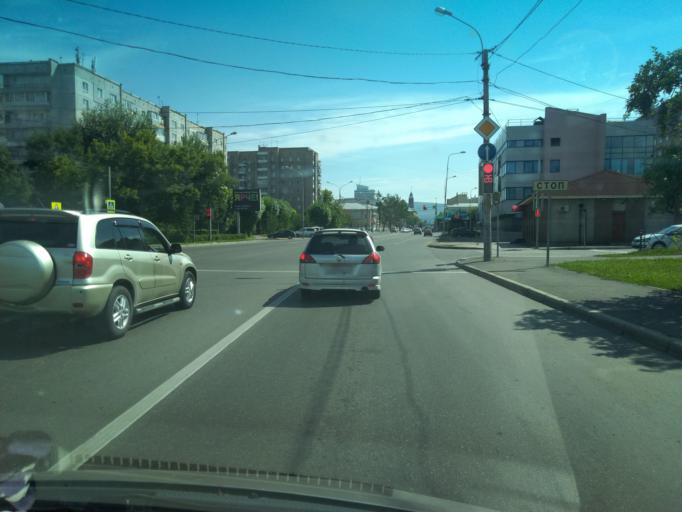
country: RU
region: Krasnoyarskiy
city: Krasnoyarsk
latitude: 56.0164
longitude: 92.8703
